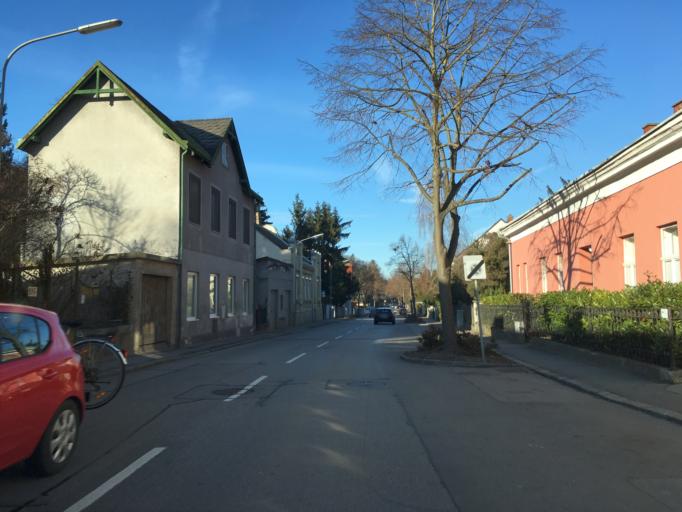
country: AT
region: Lower Austria
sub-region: Politischer Bezirk Korneuburg
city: Korneuburg
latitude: 48.3373
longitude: 16.2968
